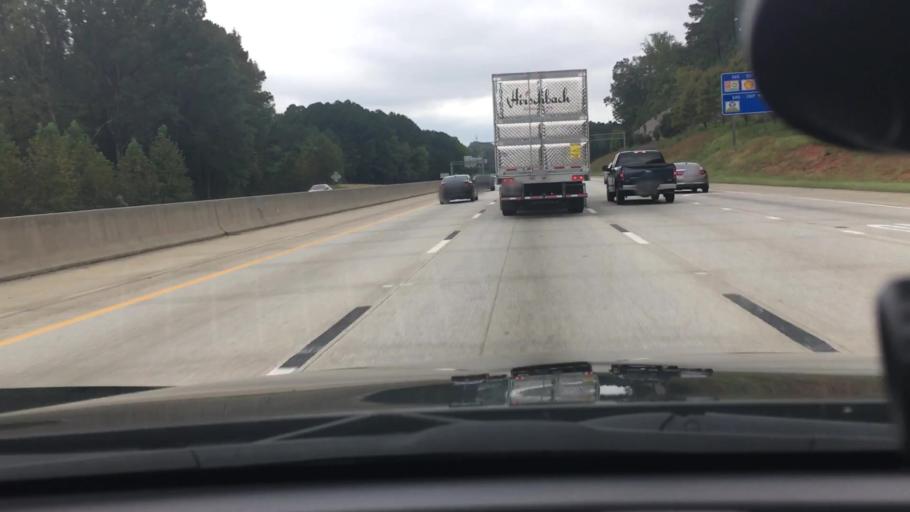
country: US
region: North Carolina
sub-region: Wake County
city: Cary
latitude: 35.7404
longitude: -78.7872
